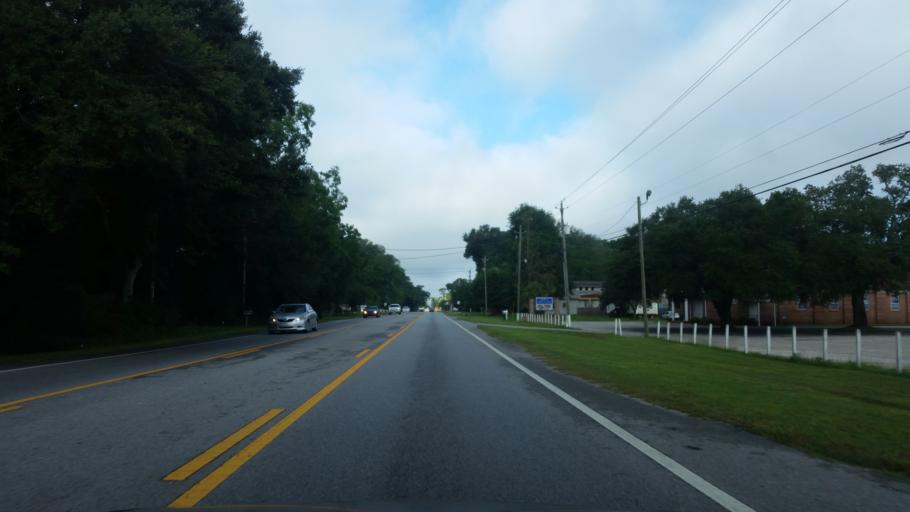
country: US
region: Florida
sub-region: Escambia County
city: Bellview
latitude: 30.4614
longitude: -87.3125
